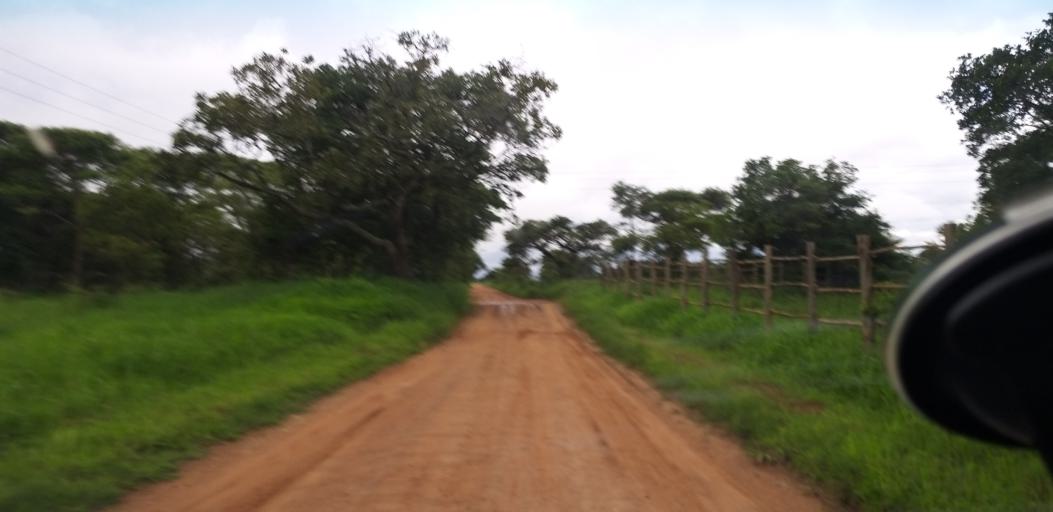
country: ZM
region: Lusaka
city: Lusaka
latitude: -15.5285
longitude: 28.3101
